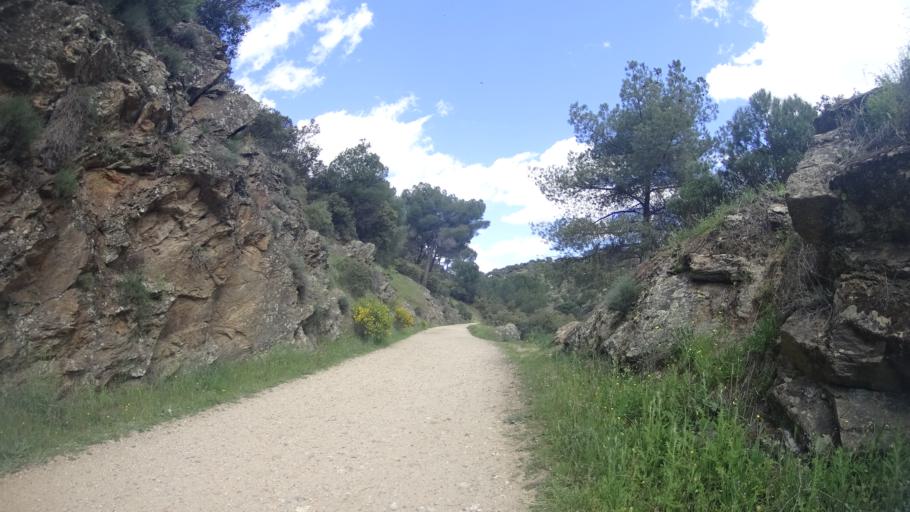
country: ES
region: Madrid
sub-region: Provincia de Madrid
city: Pelayos de la Presa
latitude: 40.3633
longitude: -4.2977
